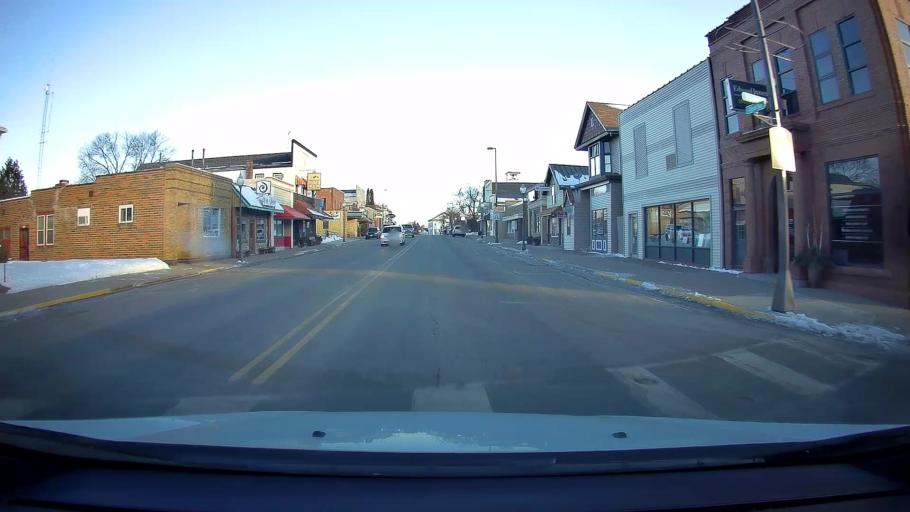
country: US
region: Wisconsin
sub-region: Barron County
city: Cumberland
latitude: 45.5339
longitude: -92.0215
